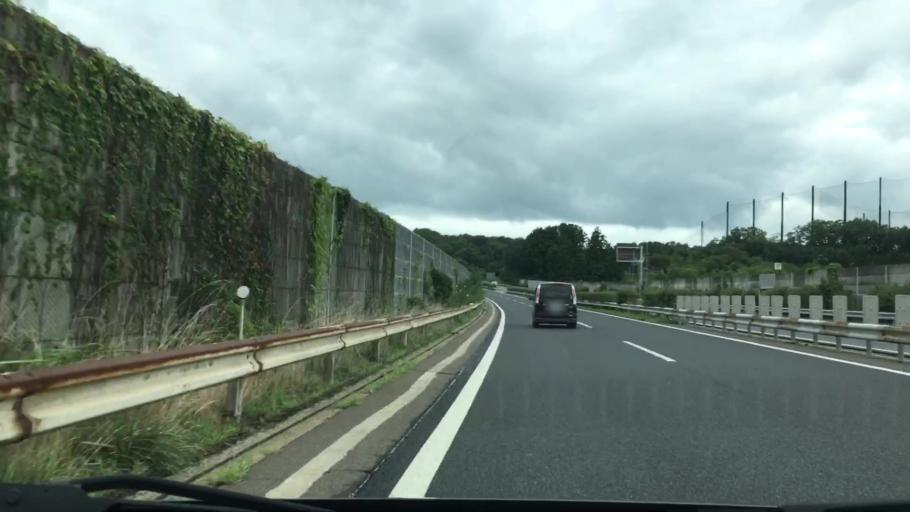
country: JP
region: Okayama
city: Tsuyama
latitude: 35.0680
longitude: 134.0435
